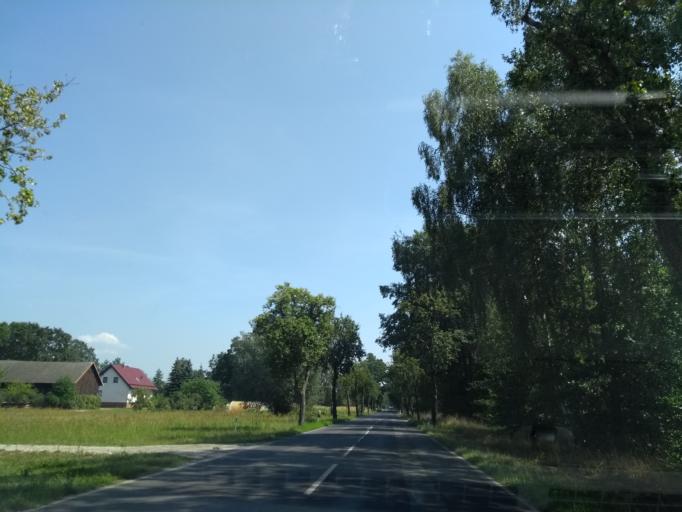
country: DE
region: Brandenburg
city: Burg
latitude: 51.8432
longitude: 14.1174
